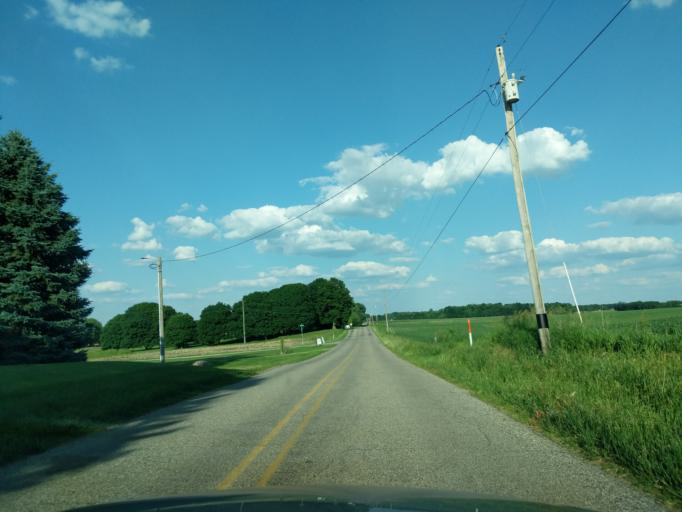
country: US
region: Indiana
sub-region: Whitley County
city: Tri-Lakes
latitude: 41.3026
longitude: -85.5341
